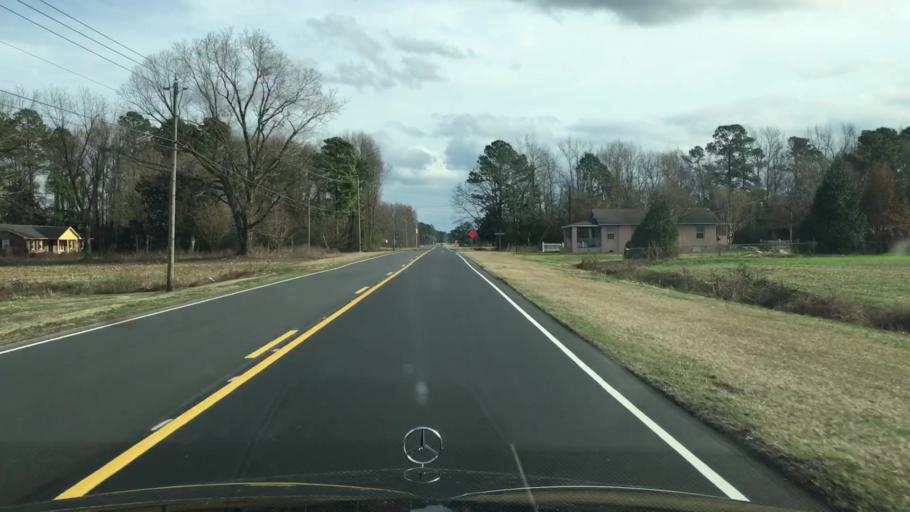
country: US
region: North Carolina
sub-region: Duplin County
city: Warsaw
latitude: 34.9813
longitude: -78.0338
